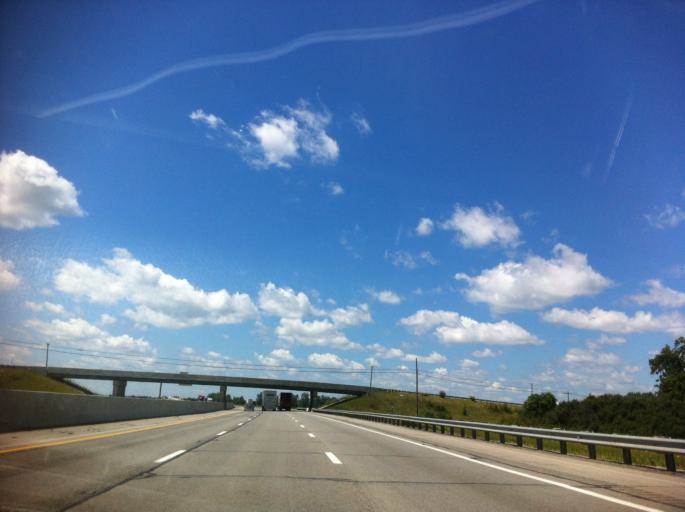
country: US
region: Ohio
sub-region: Wood County
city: Walbridge
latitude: 41.5369
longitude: -83.4905
